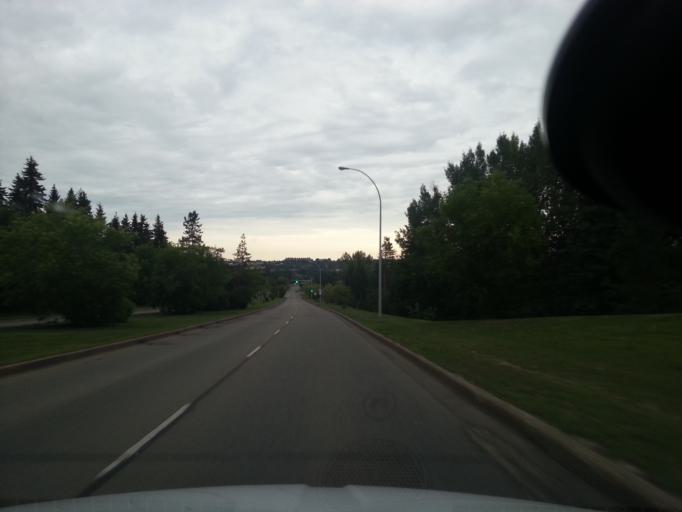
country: CA
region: Alberta
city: St. Albert
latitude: 53.6421
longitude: -113.6032
